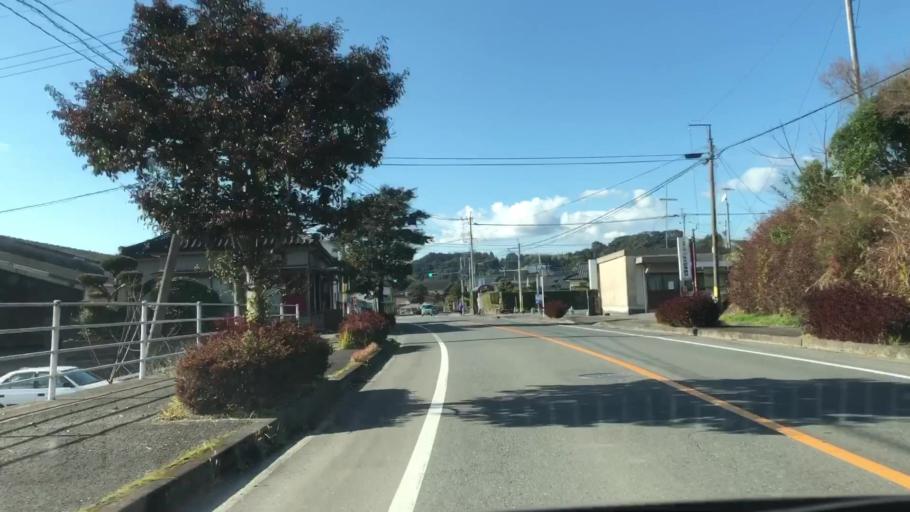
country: JP
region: Kagoshima
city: Satsumasendai
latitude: 31.8013
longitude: 130.4363
